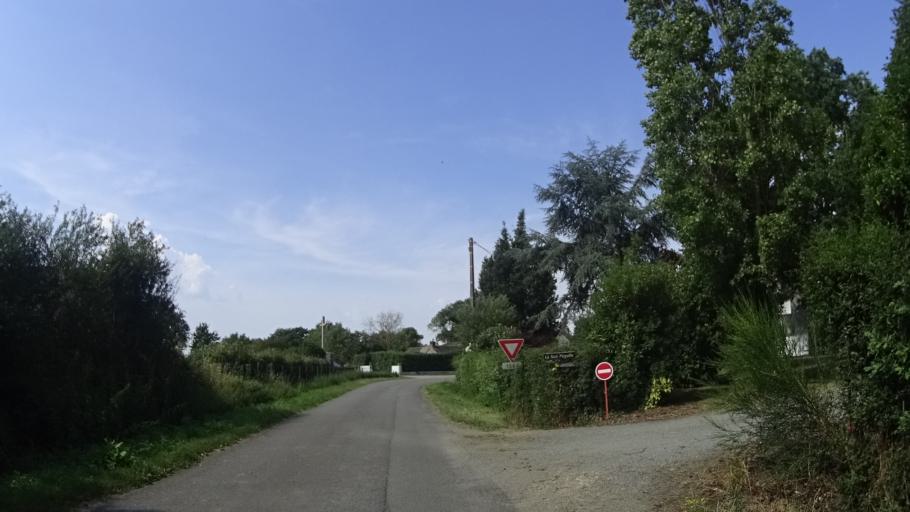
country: FR
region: Pays de la Loire
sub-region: Departement de la Loire-Atlantique
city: Saffre
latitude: 47.4788
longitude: -1.6180
